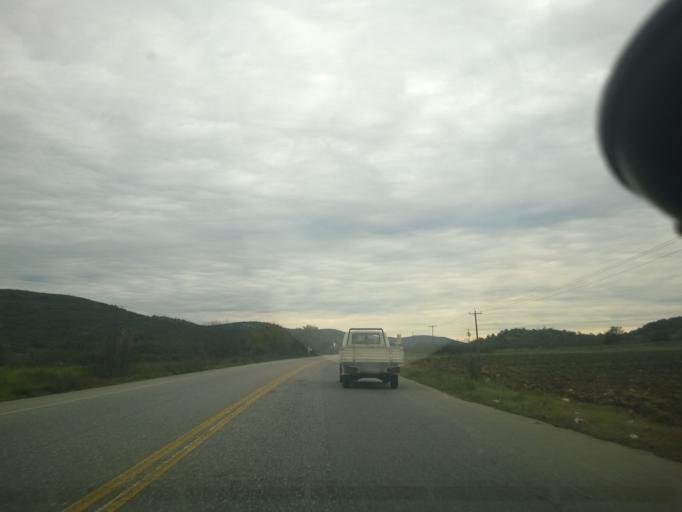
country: GR
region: Central Macedonia
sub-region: Nomos Pellis
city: Apsalos
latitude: 40.8845
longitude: 22.0781
